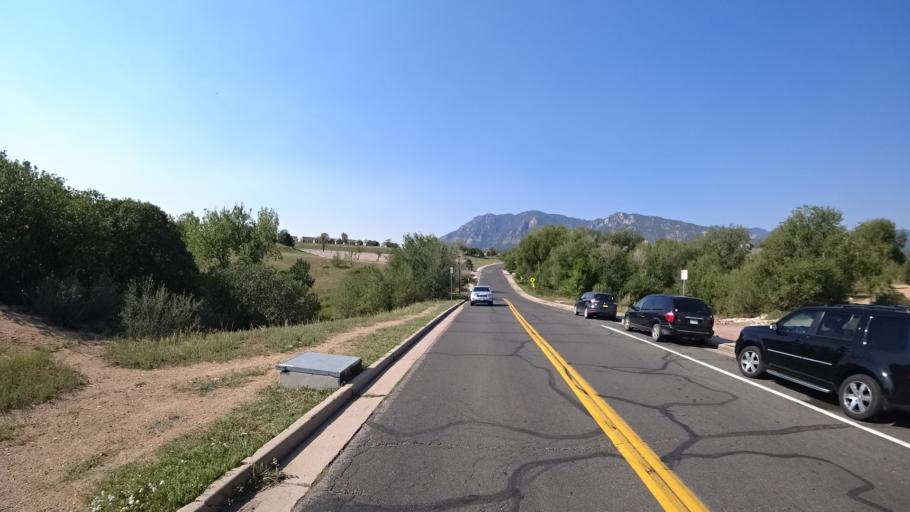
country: US
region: Colorado
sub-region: El Paso County
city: Stratmoor
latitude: 38.7843
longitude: -104.8058
